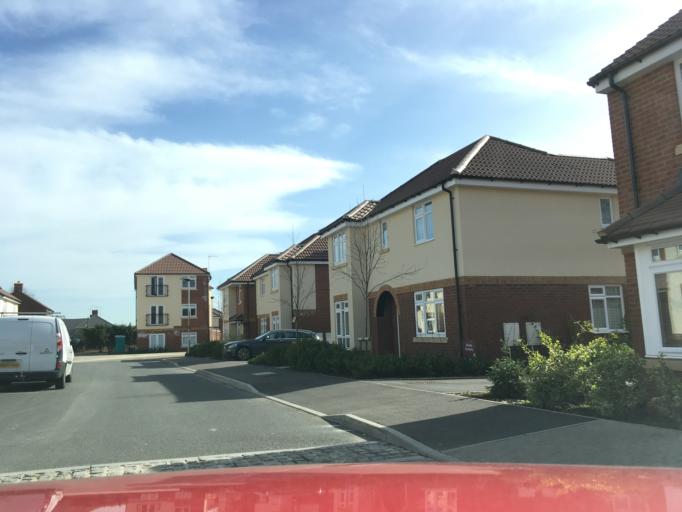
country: GB
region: England
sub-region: Wiltshire
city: Chippenham
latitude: 51.4638
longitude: -2.1328
